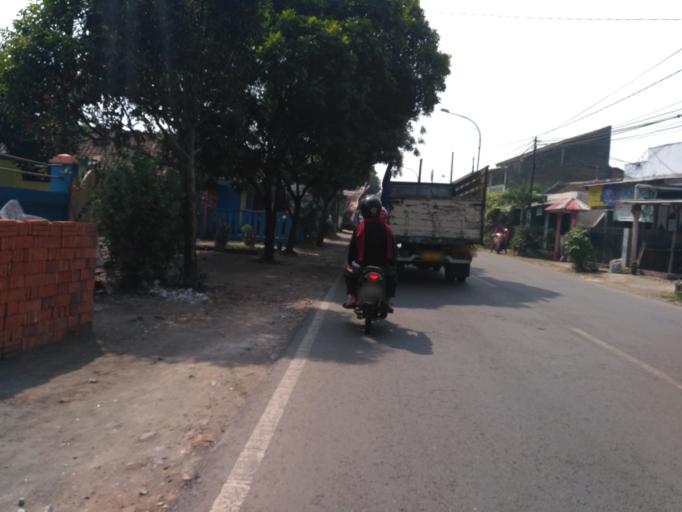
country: ID
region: East Java
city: Malang
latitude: -7.9841
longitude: 112.6594
